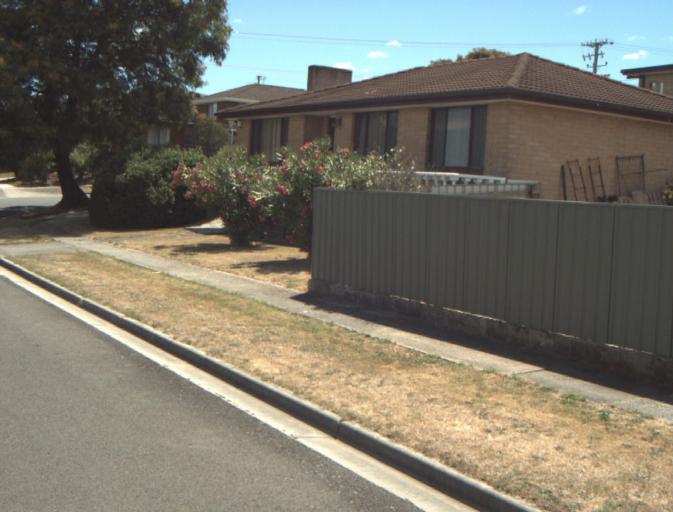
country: AU
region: Tasmania
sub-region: Launceston
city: Mayfield
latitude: -41.3854
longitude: 147.1163
